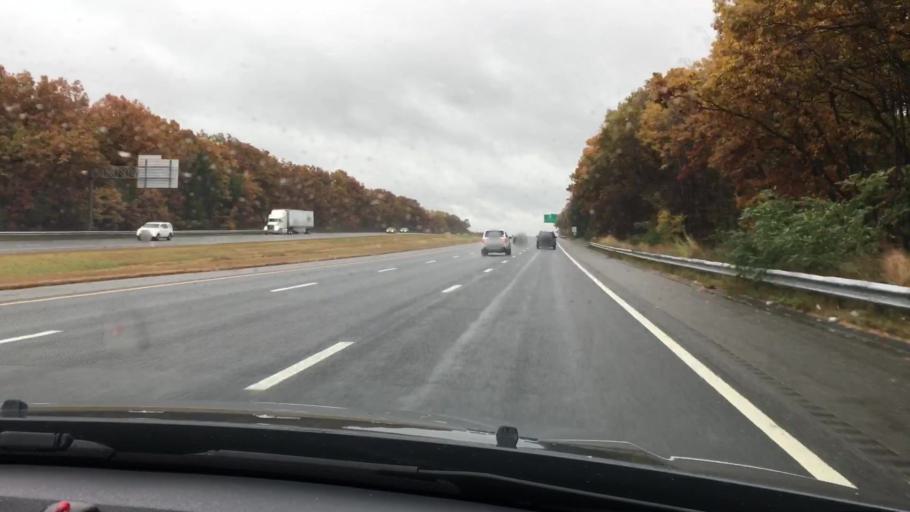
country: US
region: Massachusetts
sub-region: Middlesex County
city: Tyngsboro
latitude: 42.6492
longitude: -71.4207
